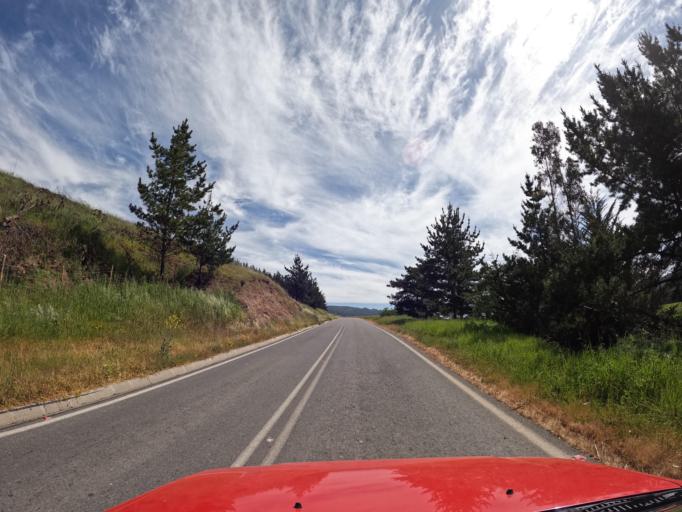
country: CL
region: Maule
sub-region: Provincia de Talca
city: Constitucion
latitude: -35.0390
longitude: -72.0580
